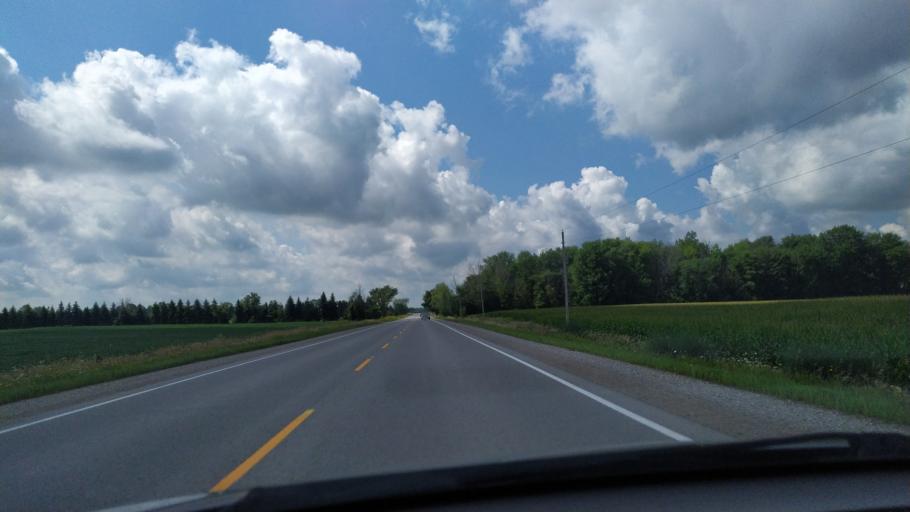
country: CA
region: Ontario
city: South Huron
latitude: 43.2821
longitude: -81.3485
